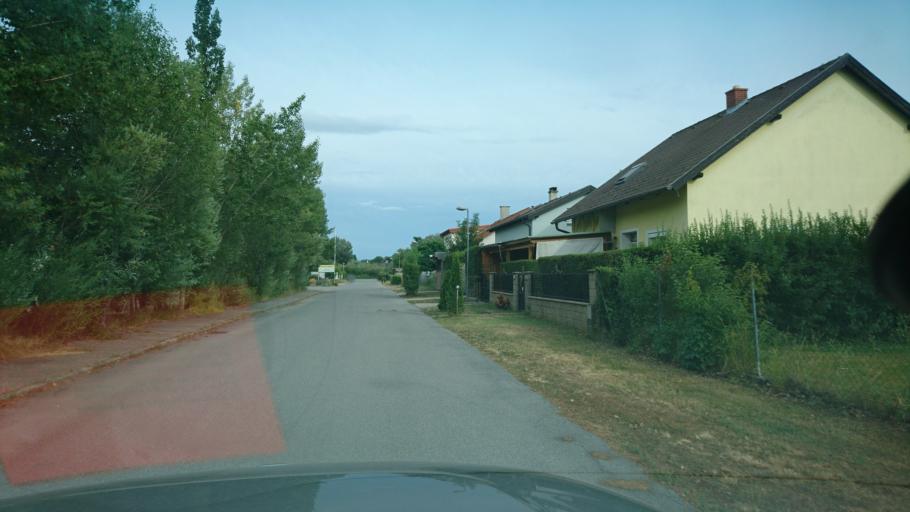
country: AT
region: Burgenland
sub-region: Politischer Bezirk Neusiedl am See
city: Neusiedl am See
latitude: 47.9378
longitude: 16.8461
